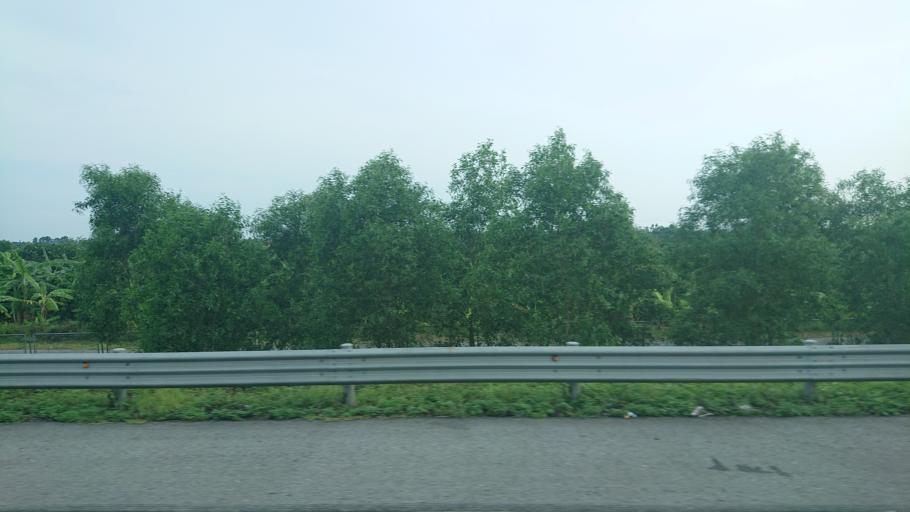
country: VN
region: Hai Duong
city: Tu Ky
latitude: 20.8302
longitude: 106.4496
